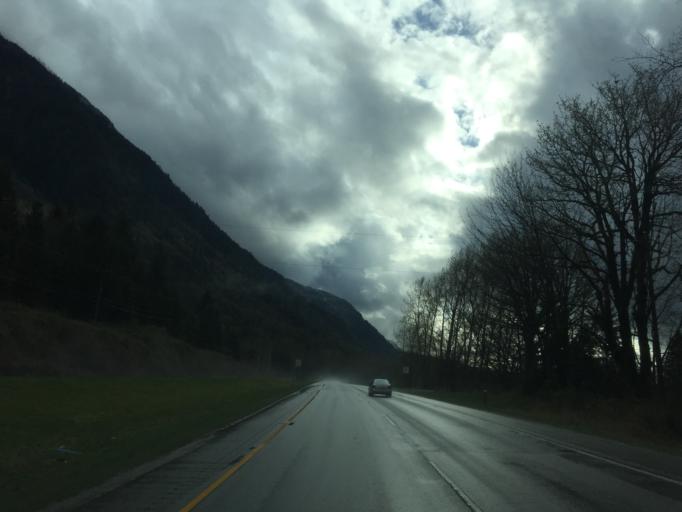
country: CA
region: British Columbia
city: Agassiz
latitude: 49.2121
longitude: -121.7054
